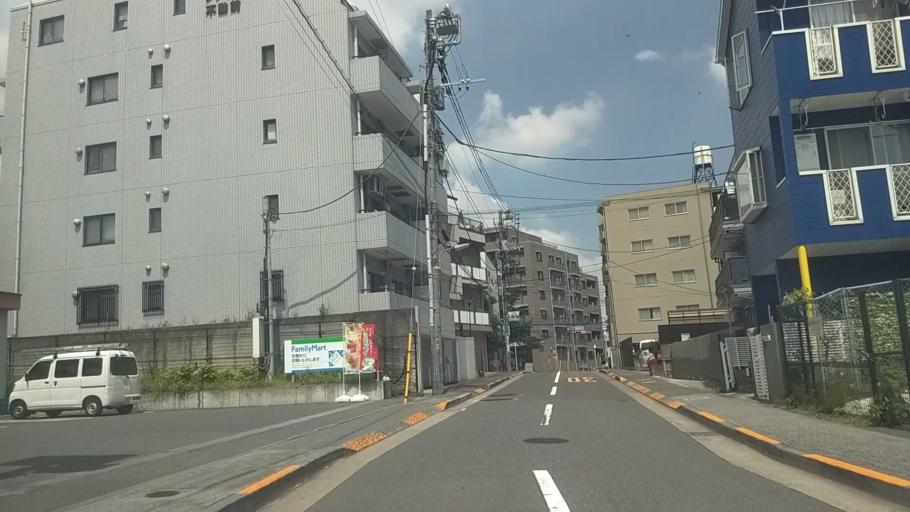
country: JP
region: Tokyo
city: Tokyo
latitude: 35.6239
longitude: 139.7108
